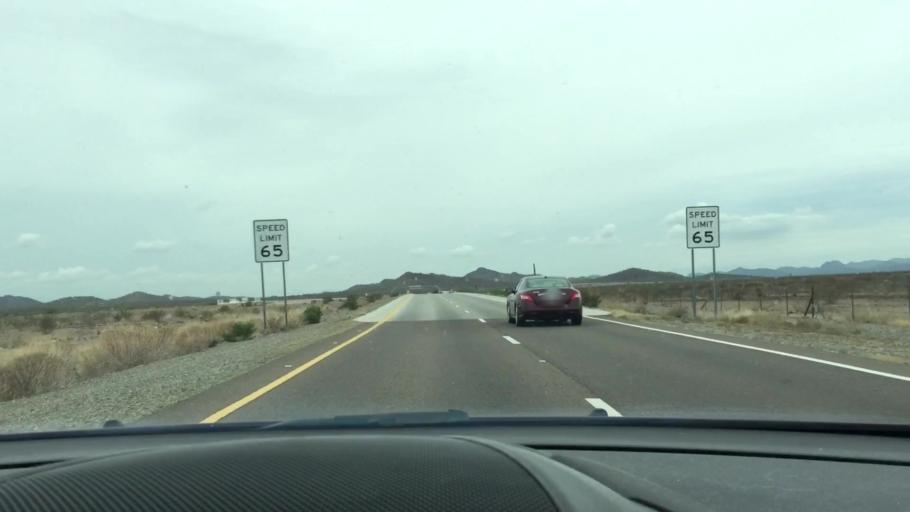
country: US
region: Arizona
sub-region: Maricopa County
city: Anthem
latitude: 33.7698
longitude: -112.1534
